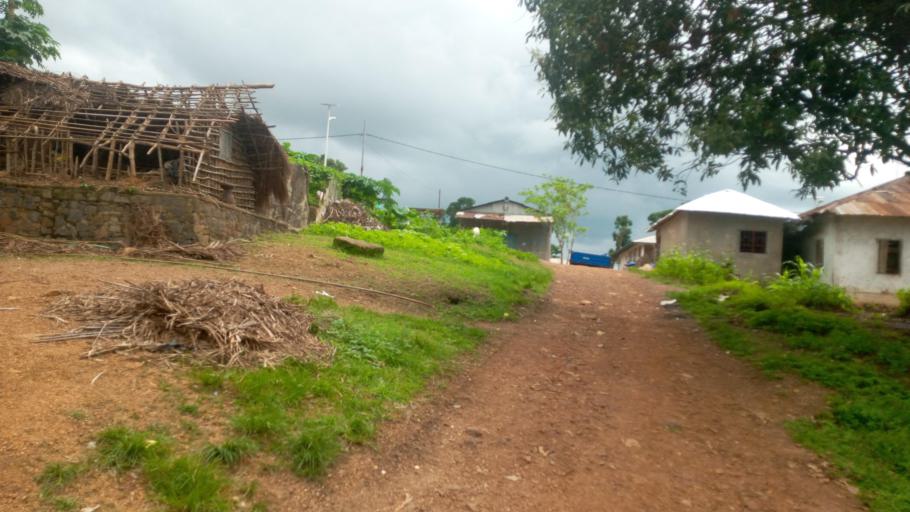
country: SL
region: Southern Province
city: Mogbwemo
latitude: 7.6054
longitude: -12.1765
